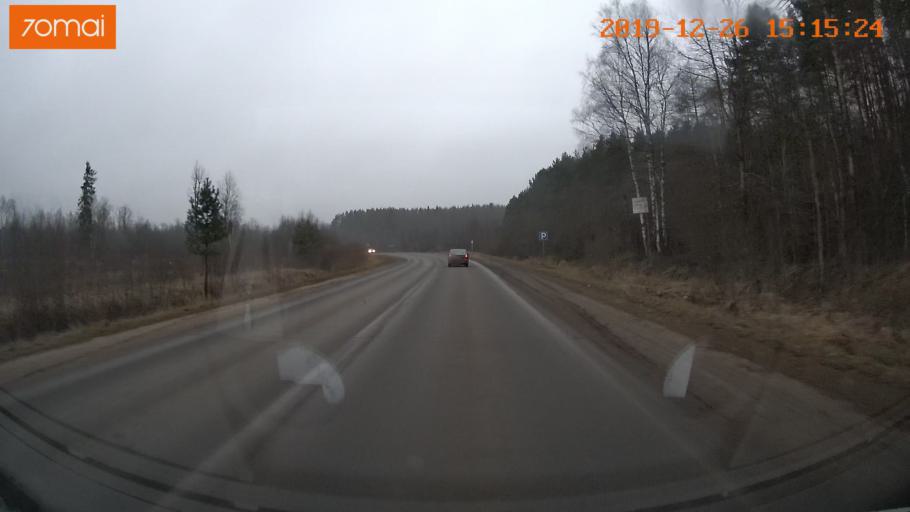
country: RU
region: Jaroslavl
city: Rybinsk
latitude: 58.0972
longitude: 38.8751
